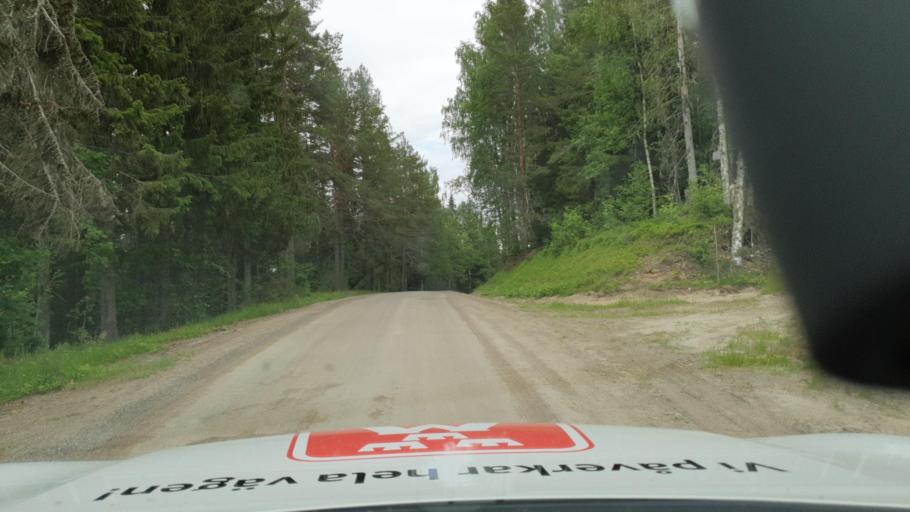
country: SE
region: Vaesterbotten
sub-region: Nordmalings Kommun
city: Nordmaling
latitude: 63.6794
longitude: 19.4457
